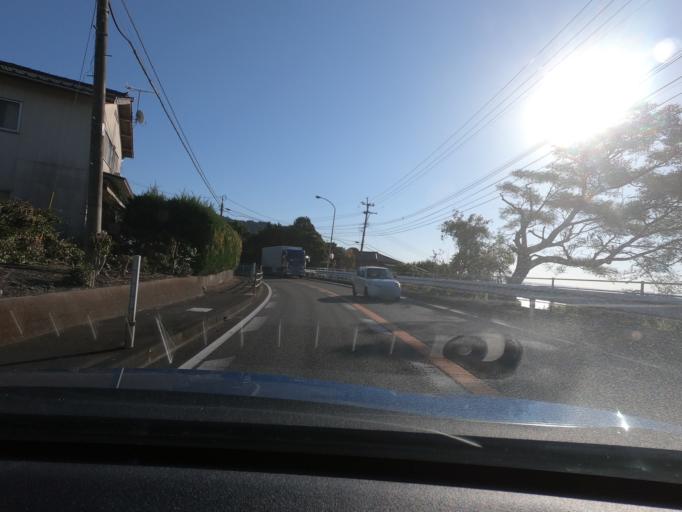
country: JP
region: Kumamoto
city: Minamata
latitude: 32.1562
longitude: 130.3634
